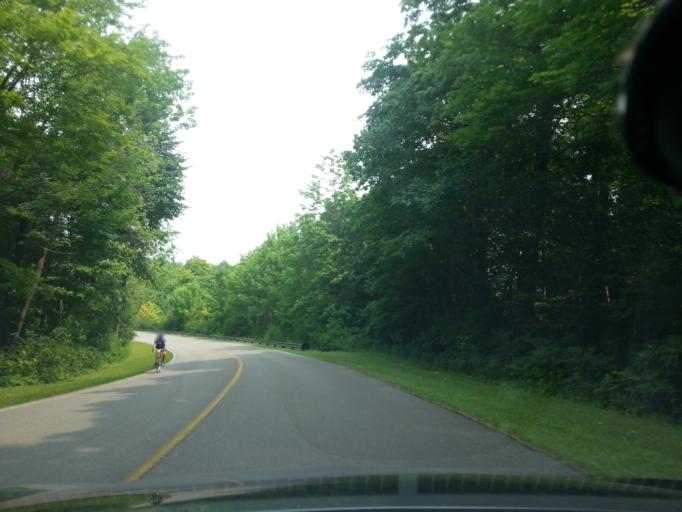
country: CA
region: Quebec
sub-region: Outaouais
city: Gatineau
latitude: 45.4934
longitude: -75.8312
